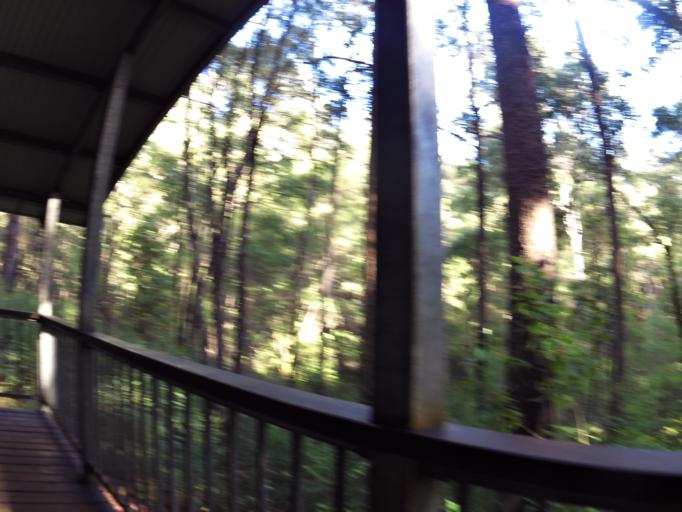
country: AU
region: Western Australia
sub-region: Donnybrook-Balingup
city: Donnybrook
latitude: -33.4098
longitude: 115.9276
